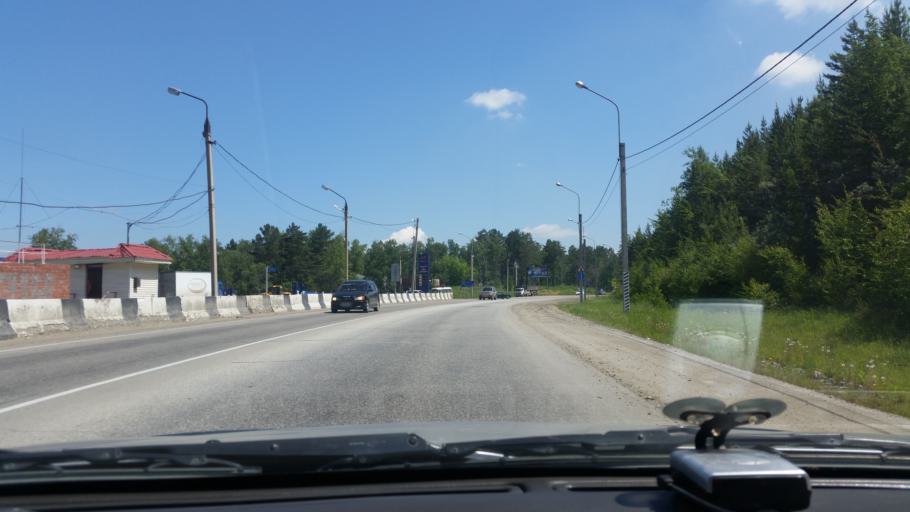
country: RU
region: Irkutsk
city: Smolenshchina
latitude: 52.2519
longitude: 104.1589
